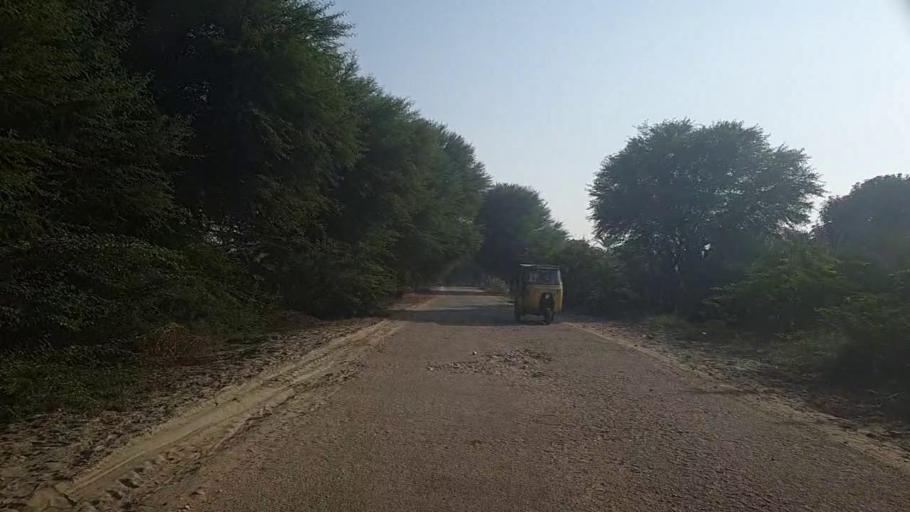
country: PK
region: Sindh
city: Bozdar
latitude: 27.2560
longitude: 68.6765
